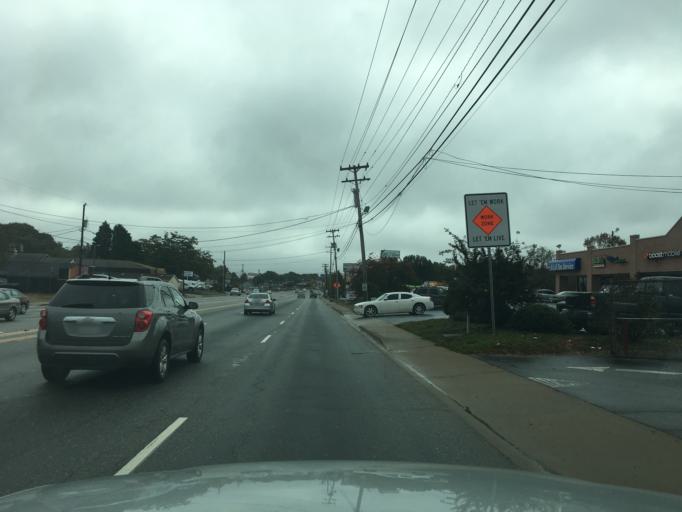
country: US
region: South Carolina
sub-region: Greenville County
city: Welcome
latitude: 34.8198
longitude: -82.4447
